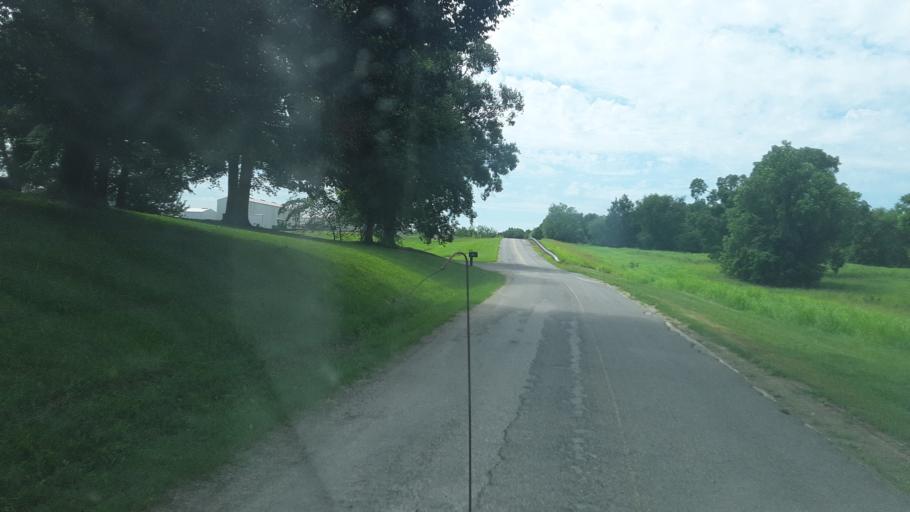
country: US
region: Kentucky
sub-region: Christian County
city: Oak Grove
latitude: 36.6484
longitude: -87.3439
